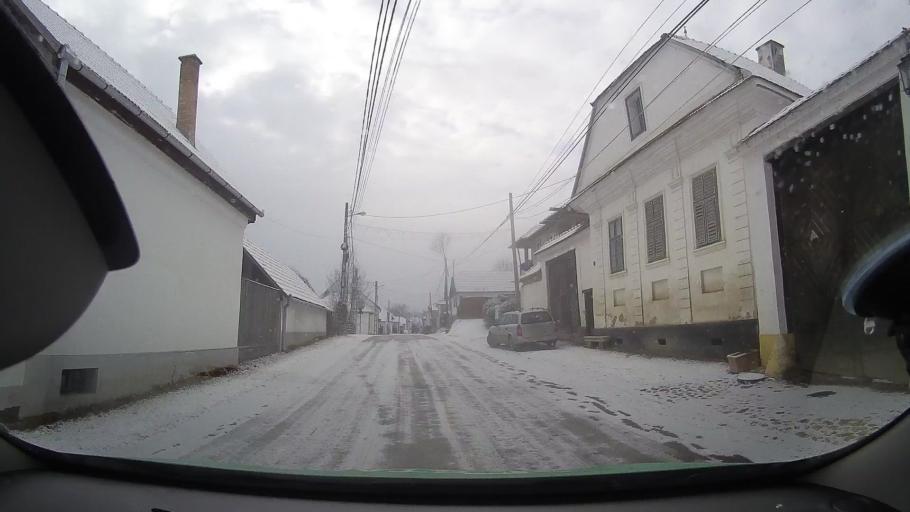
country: RO
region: Alba
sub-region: Comuna Rimetea
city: Rimetea
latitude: 46.4515
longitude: 23.5668
